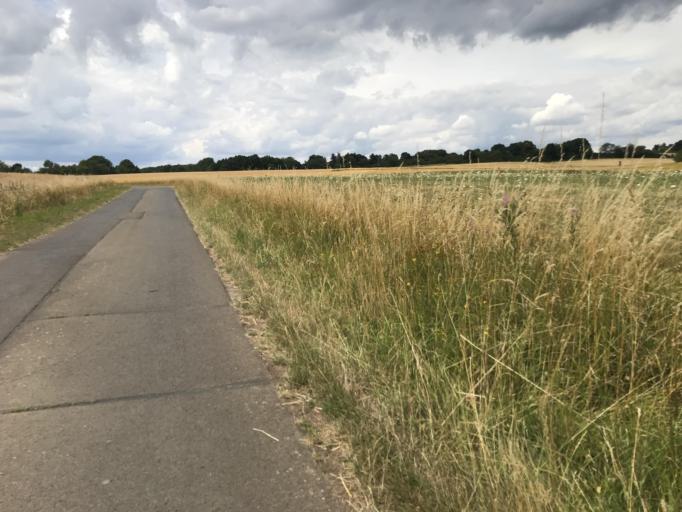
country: DE
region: Hesse
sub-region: Regierungsbezirk Giessen
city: Grunberg
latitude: 50.5758
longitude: 8.9007
